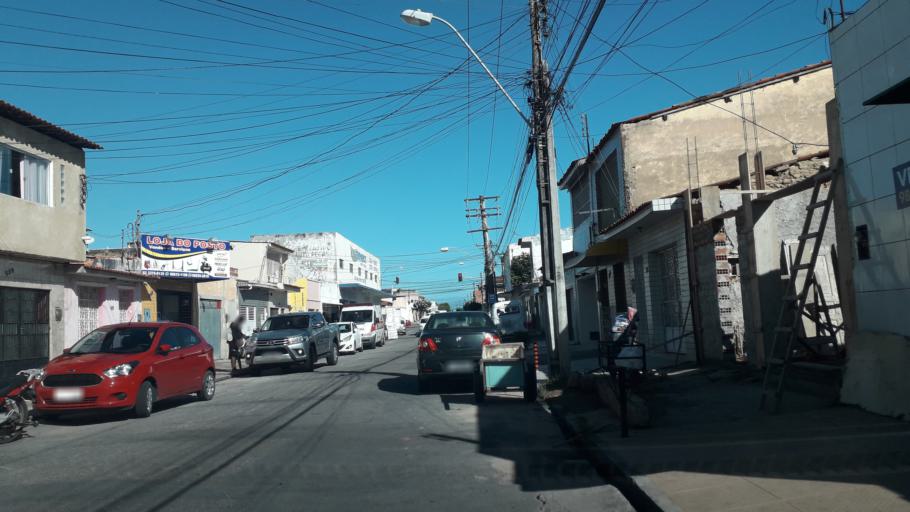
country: BR
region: Alagoas
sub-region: Maceio
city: Maceio
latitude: -9.6685
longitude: -35.7502
